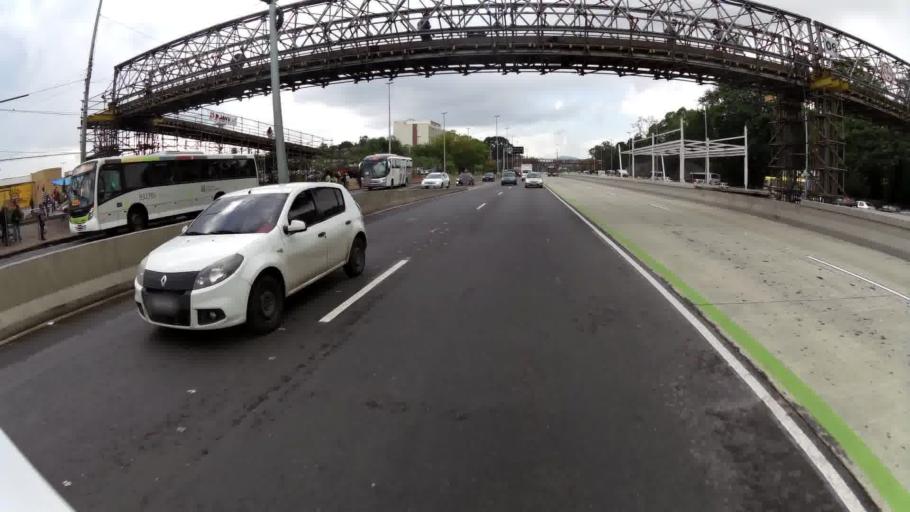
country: BR
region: Rio de Janeiro
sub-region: Rio De Janeiro
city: Rio de Janeiro
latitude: -22.8753
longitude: -43.2429
